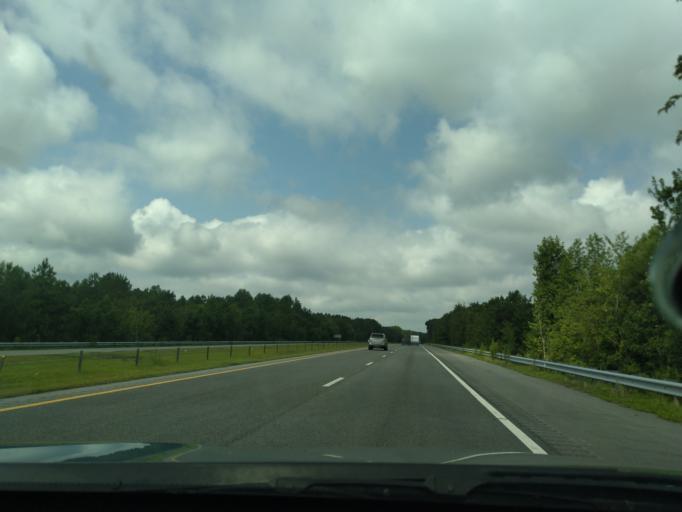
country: US
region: North Carolina
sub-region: Martin County
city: Robersonville
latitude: 35.8329
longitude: -77.2831
